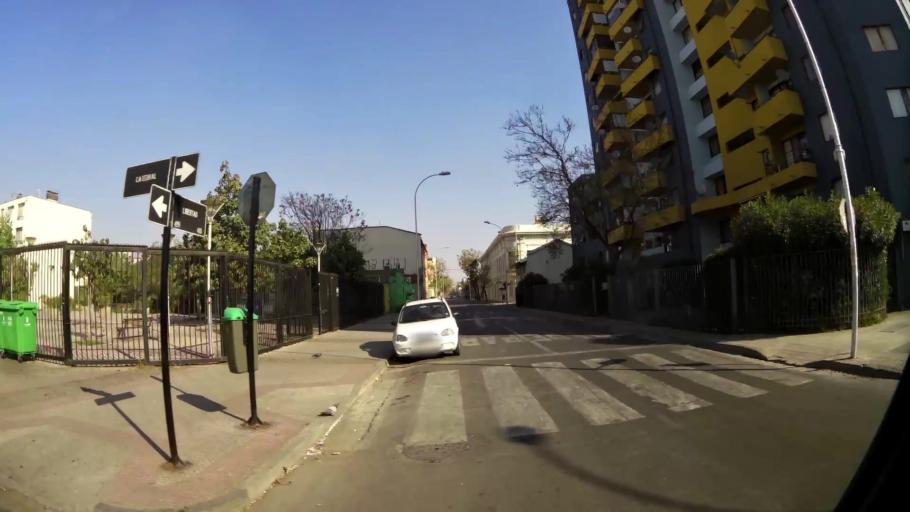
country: CL
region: Santiago Metropolitan
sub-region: Provincia de Santiago
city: Santiago
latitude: -33.4399
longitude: -70.6744
